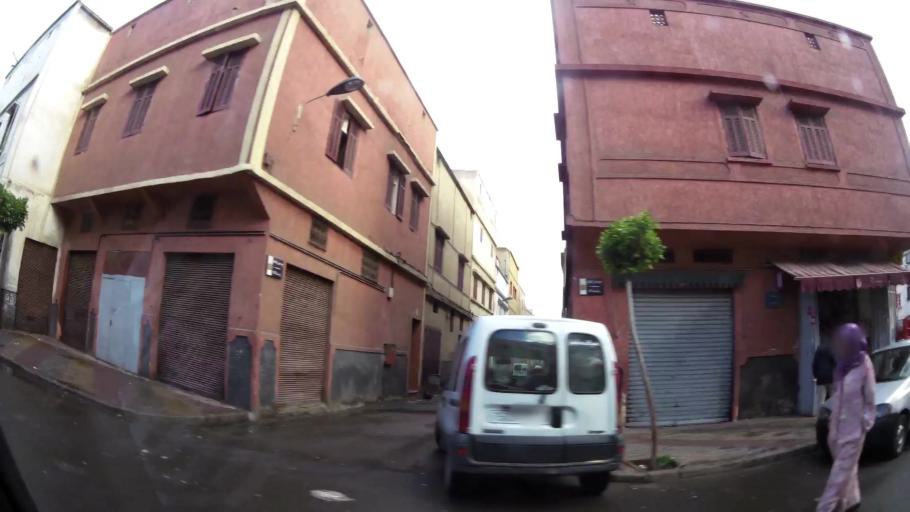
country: MA
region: Grand Casablanca
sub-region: Casablanca
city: Casablanca
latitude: 33.5637
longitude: -7.5836
